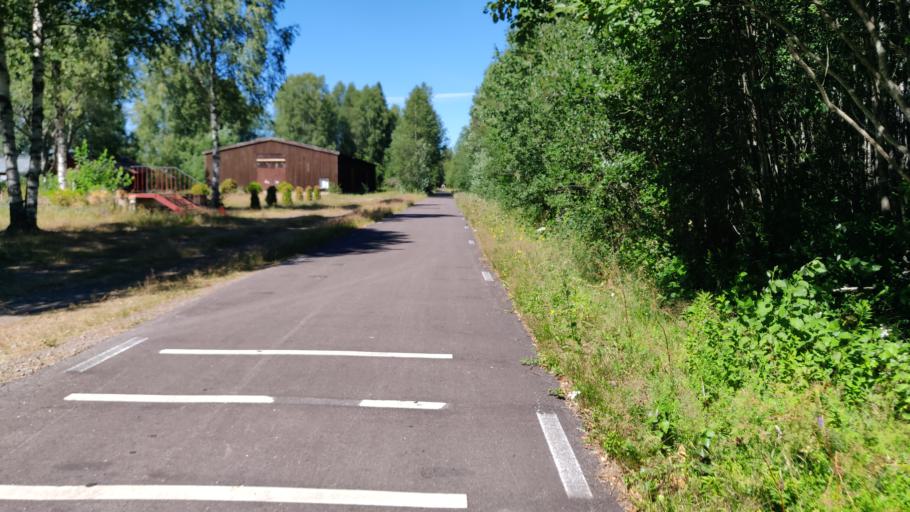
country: SE
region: Vaermland
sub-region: Hagfors Kommun
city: Hagfors
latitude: 59.9663
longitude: 13.5721
